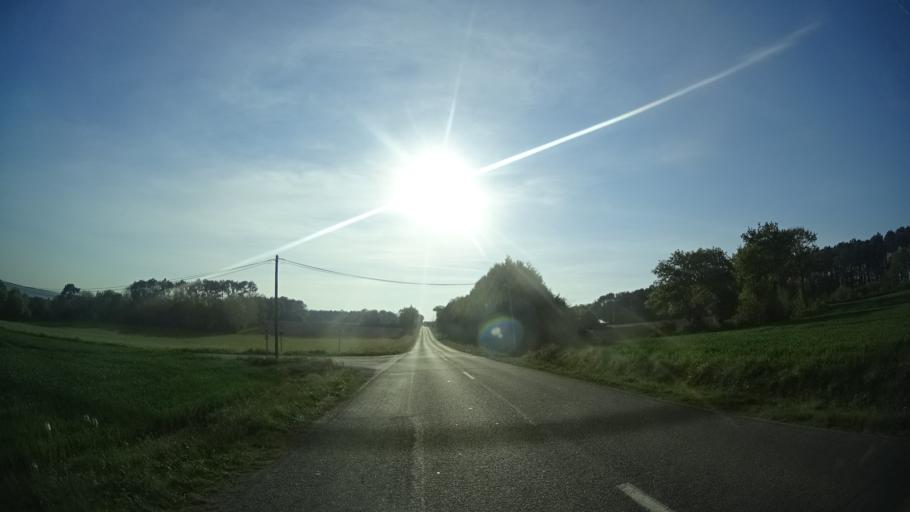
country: FR
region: Brittany
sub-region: Departement du Morbihan
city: Allaire
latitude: 47.6118
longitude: -2.1684
